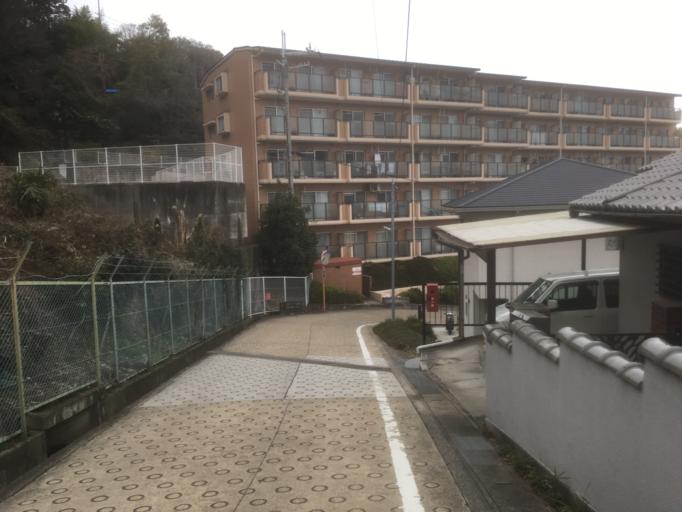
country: JP
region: Nara
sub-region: Ikoma-shi
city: Ikoma
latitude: 34.6860
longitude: 135.6930
